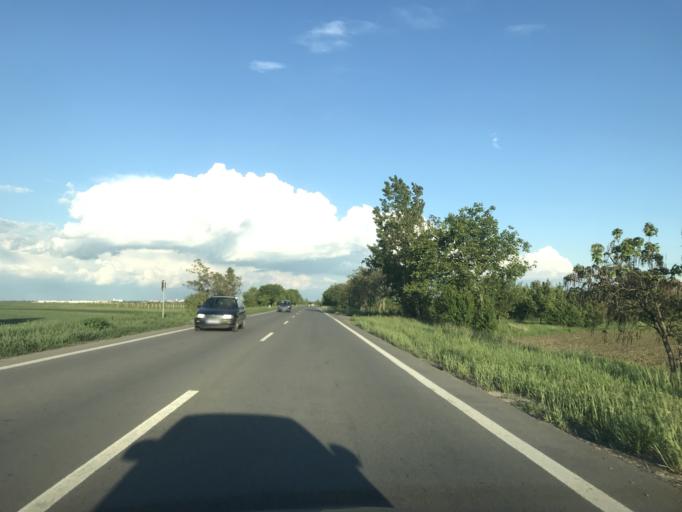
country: RS
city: Aradac
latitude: 45.3884
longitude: 20.3112
